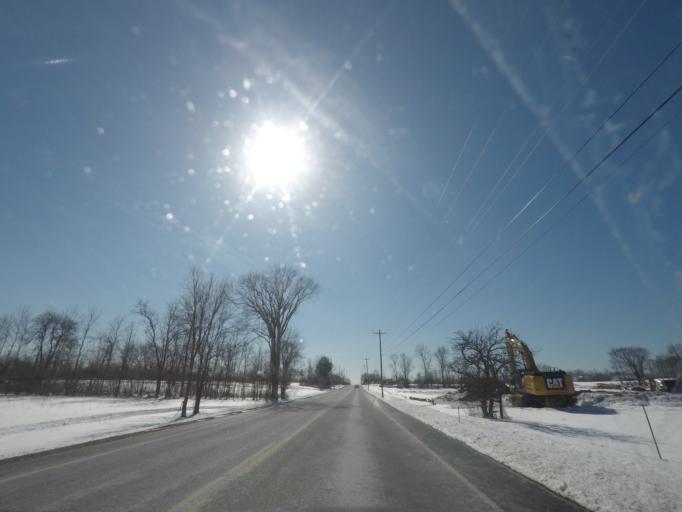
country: US
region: New York
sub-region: Saratoga County
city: Country Knolls
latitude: 42.9568
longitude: -73.8286
